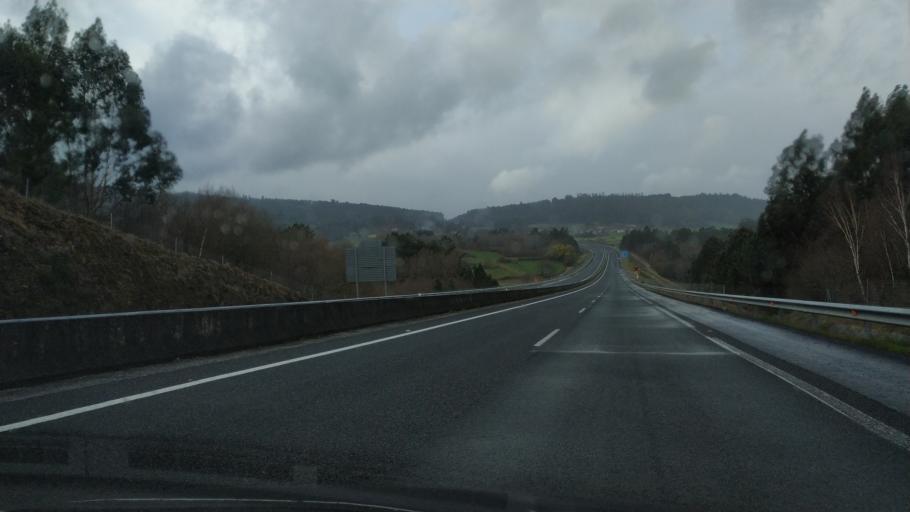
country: ES
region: Galicia
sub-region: Provincia de Pontevedra
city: Silleda
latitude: 42.7244
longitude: -8.3181
